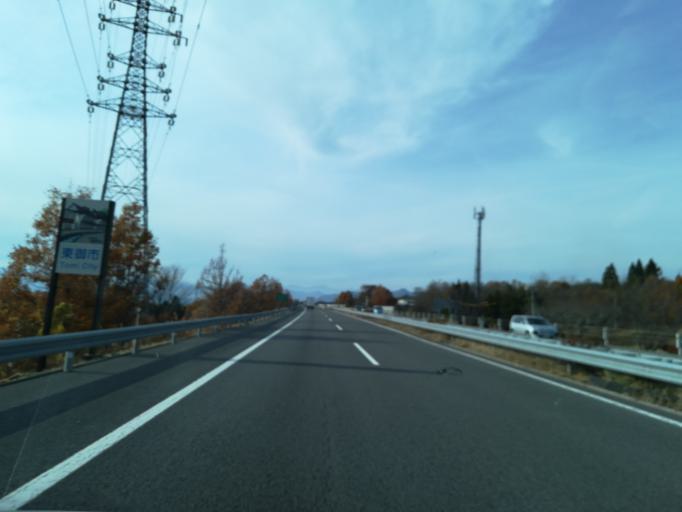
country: JP
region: Nagano
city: Komoro
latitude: 36.3510
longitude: 138.3853
